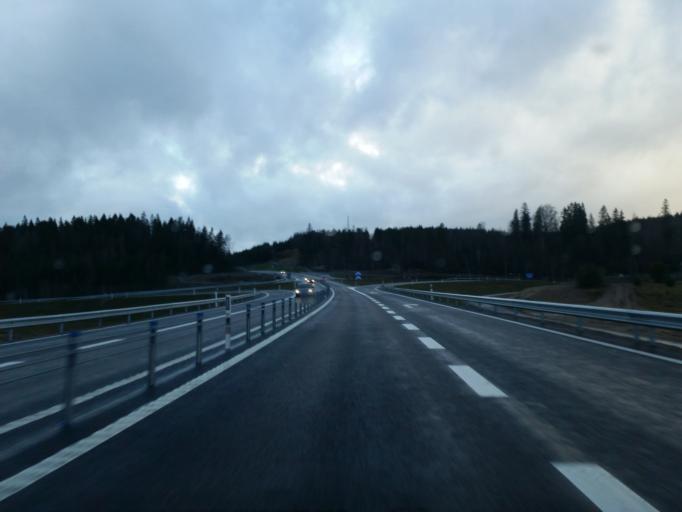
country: SE
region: Vaestra Goetaland
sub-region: Boras Kommun
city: Boras
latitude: 57.6977
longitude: 12.9117
